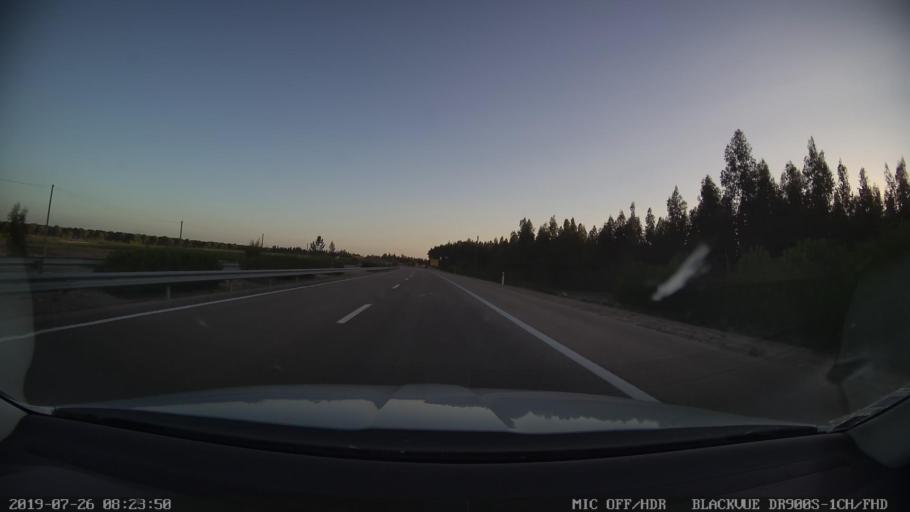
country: PT
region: Evora
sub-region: Vendas Novas
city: Vendas Novas
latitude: 38.6630
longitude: -8.6571
